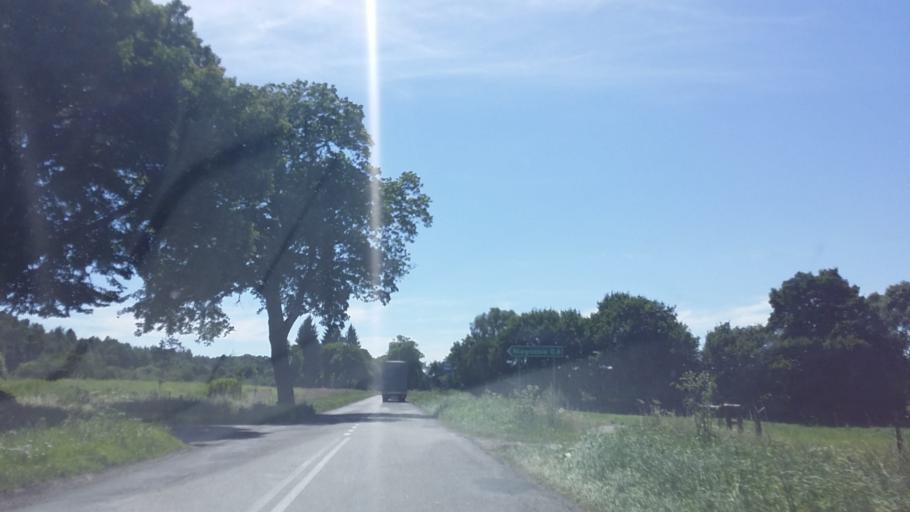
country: PL
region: West Pomeranian Voivodeship
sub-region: Powiat lobeski
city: Lobez
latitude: 53.6493
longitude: 15.6401
